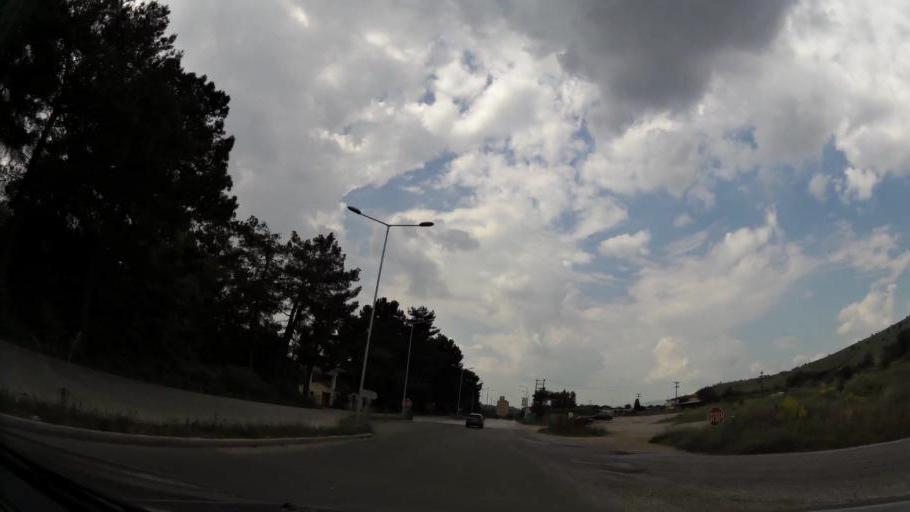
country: GR
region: West Macedonia
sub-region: Nomos Kozanis
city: Koila
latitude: 40.3339
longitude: 21.8263
